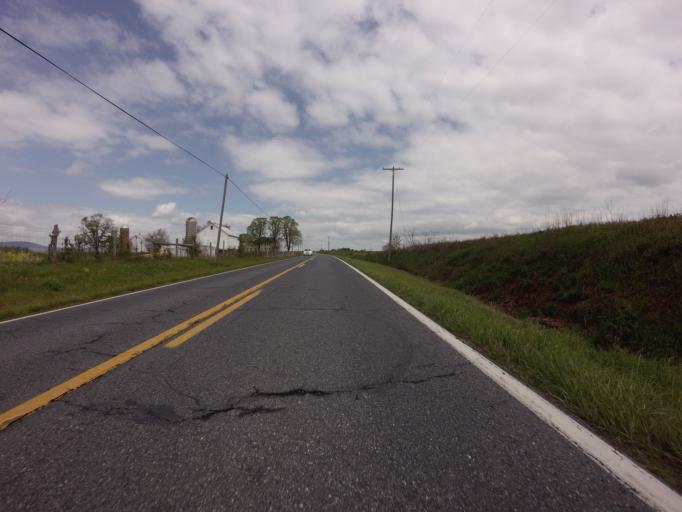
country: US
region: Maryland
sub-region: Frederick County
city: Thurmont
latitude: 39.5931
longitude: -77.3592
